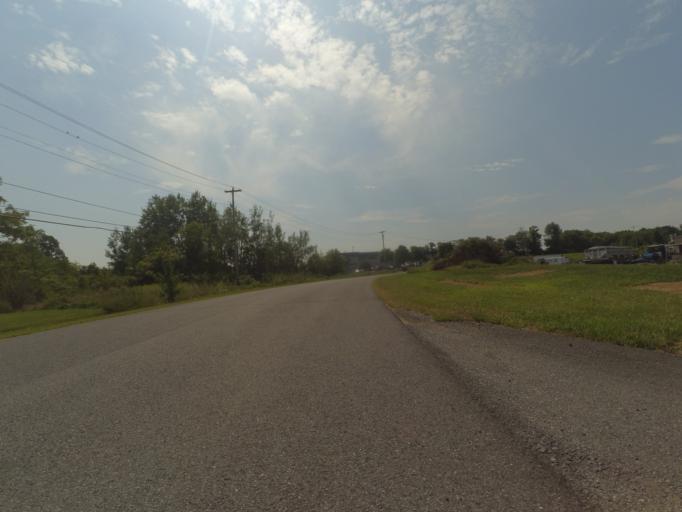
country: US
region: Pennsylvania
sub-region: Centre County
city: Bellefonte
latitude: 40.8878
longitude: -77.7687
